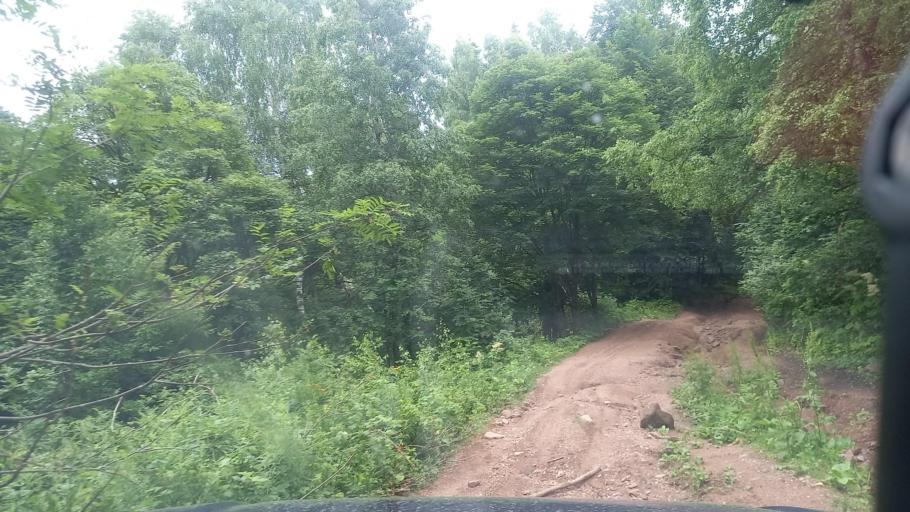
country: RU
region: Karachayevo-Cherkesiya
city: Kurdzhinovo
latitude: 43.8076
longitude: 40.8480
